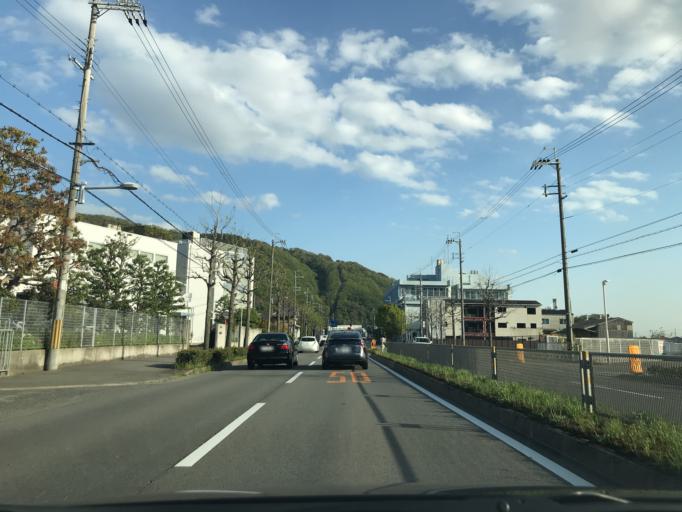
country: JP
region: Osaka
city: Ikeda
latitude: 34.8440
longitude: 135.4233
